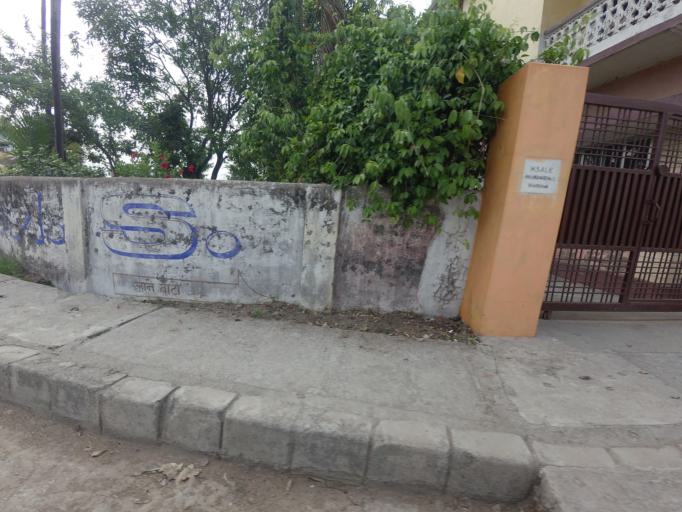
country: NP
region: Western Region
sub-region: Lumbini Zone
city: Bhairahawa
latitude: 27.4922
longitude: 83.4466
